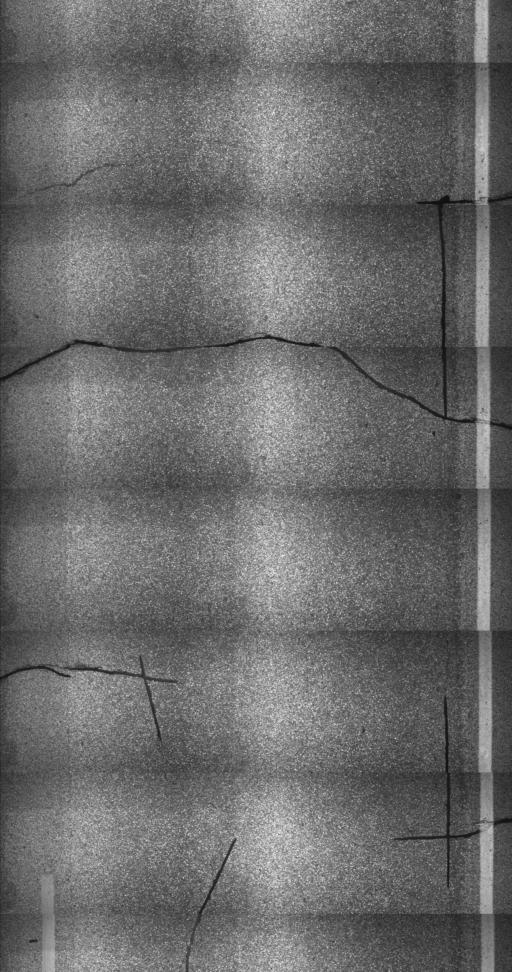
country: US
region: Vermont
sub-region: Washington County
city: Barre
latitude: 44.2395
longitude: -72.4893
